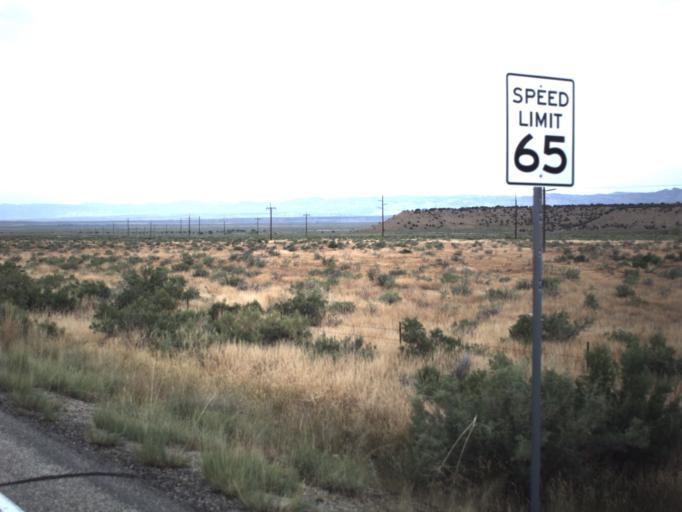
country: US
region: Utah
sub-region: Carbon County
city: East Carbon City
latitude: 39.5358
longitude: -110.4907
